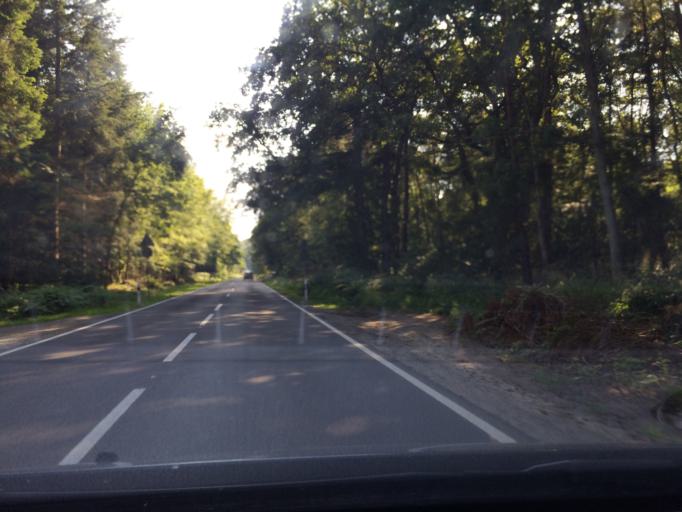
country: DE
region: Mecklenburg-Vorpommern
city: Ostseebad Binz
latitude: 54.4392
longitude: 13.5651
